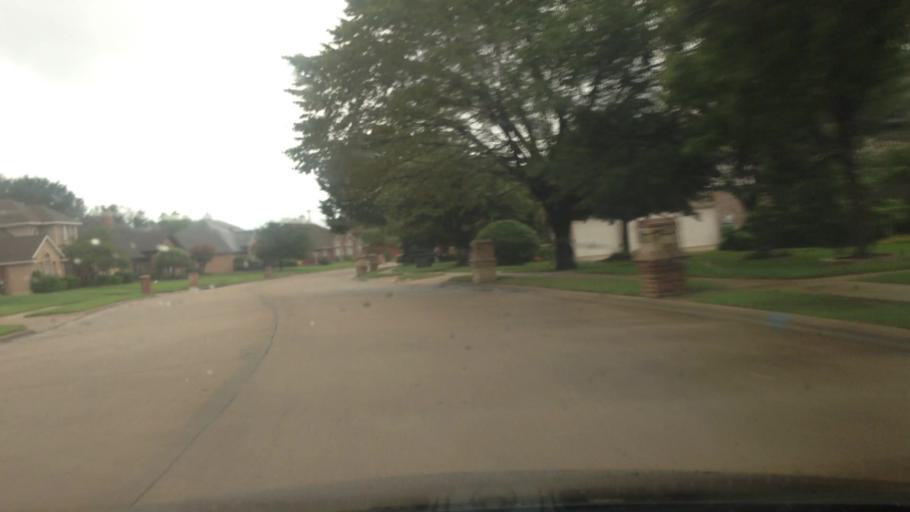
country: US
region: Texas
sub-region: Tarrant County
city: Colleyville
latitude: 32.8792
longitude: -97.1796
